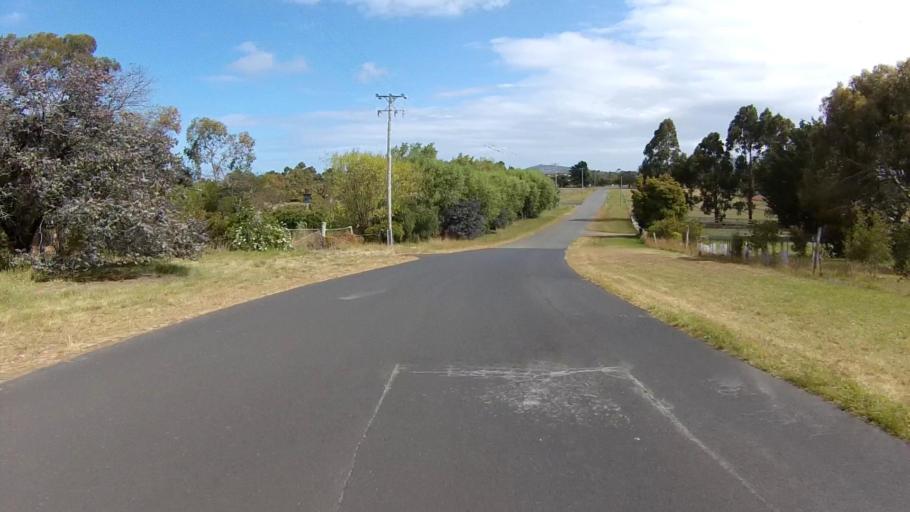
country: AU
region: Tasmania
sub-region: Clarence
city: Acton Park
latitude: -42.8869
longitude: 147.4966
